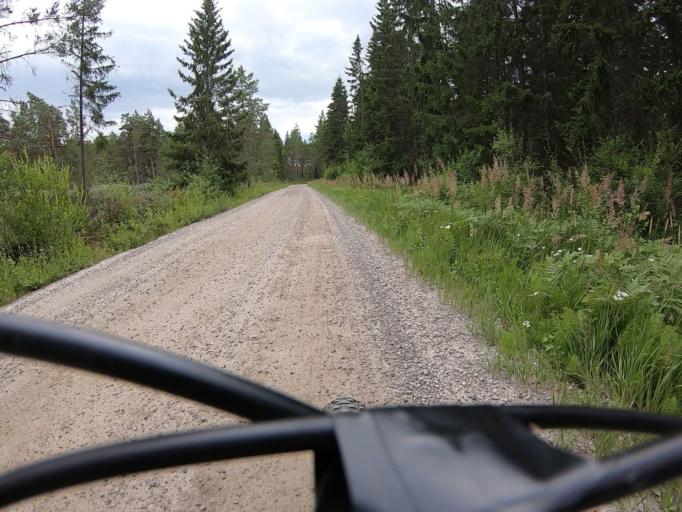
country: FI
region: Varsinais-Suomi
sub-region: Vakka-Suomi
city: Uusikaupunki
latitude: 60.8439
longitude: 21.3885
